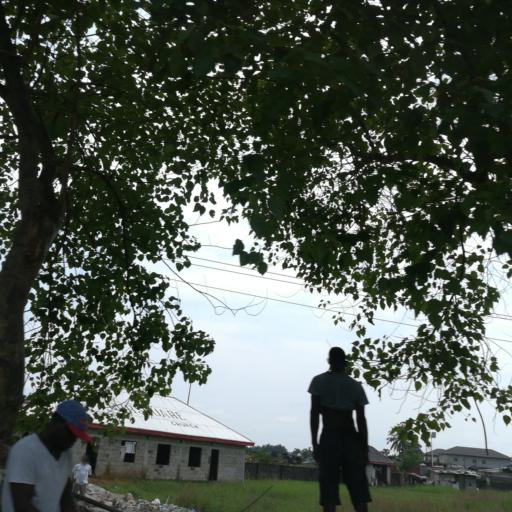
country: NG
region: Rivers
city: Port Harcourt
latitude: 4.8912
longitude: 7.0087
